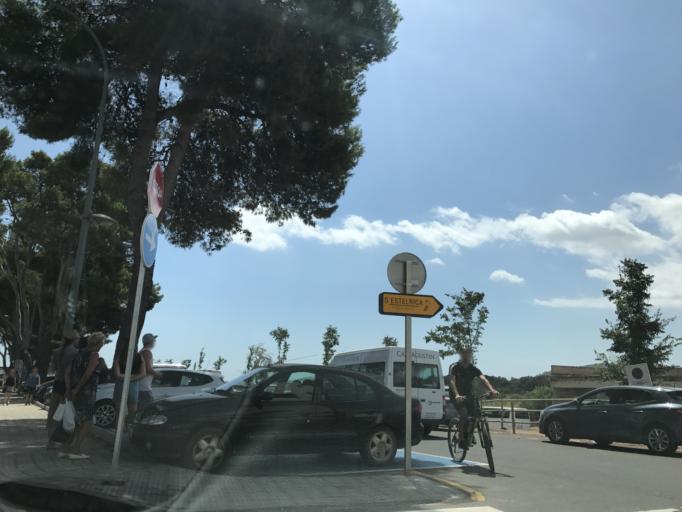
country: ES
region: Balearic Islands
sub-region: Illes Balears
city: Arta
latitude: 39.6908
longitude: 3.3517
